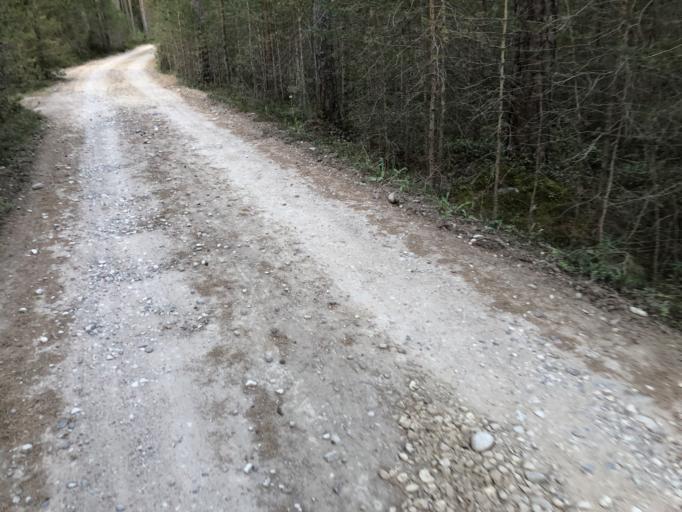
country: EE
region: Harju
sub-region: Paldiski linn
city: Paldiski
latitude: 59.3911
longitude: 24.2242
